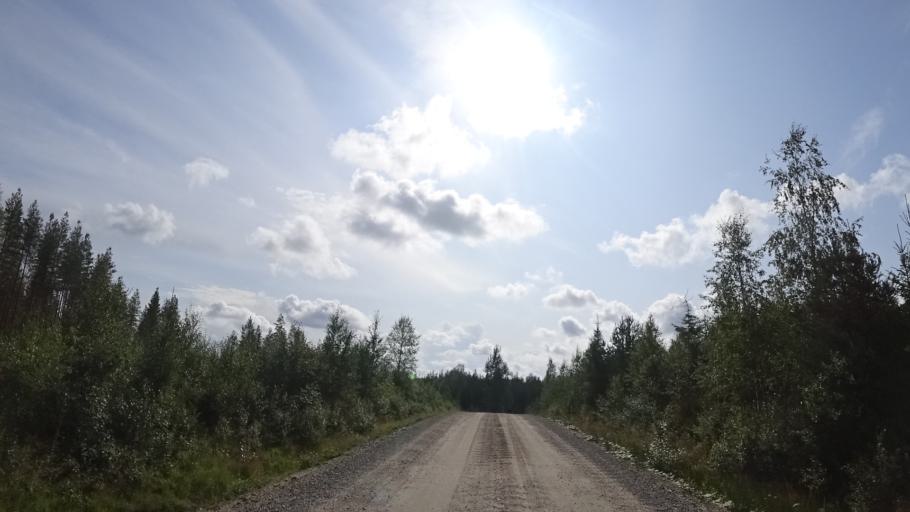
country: FI
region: North Karelia
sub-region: Pielisen Karjala
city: Lieksa
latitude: 63.5806
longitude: 30.1297
